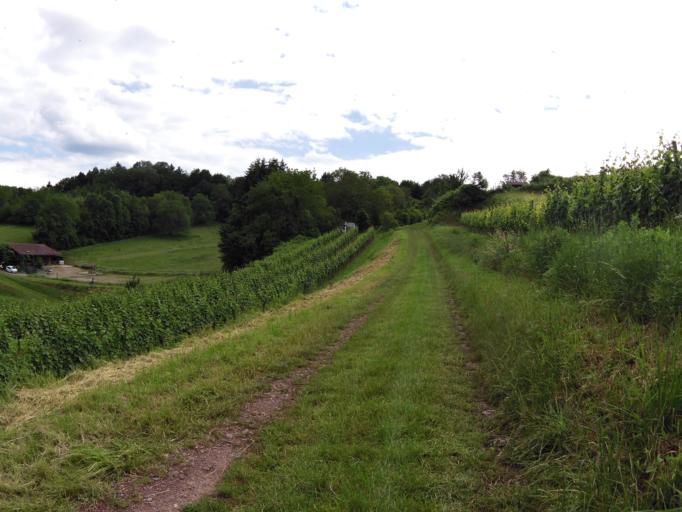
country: DE
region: Baden-Wuerttemberg
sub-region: Freiburg Region
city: Lahr
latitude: 48.3551
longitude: 7.8569
